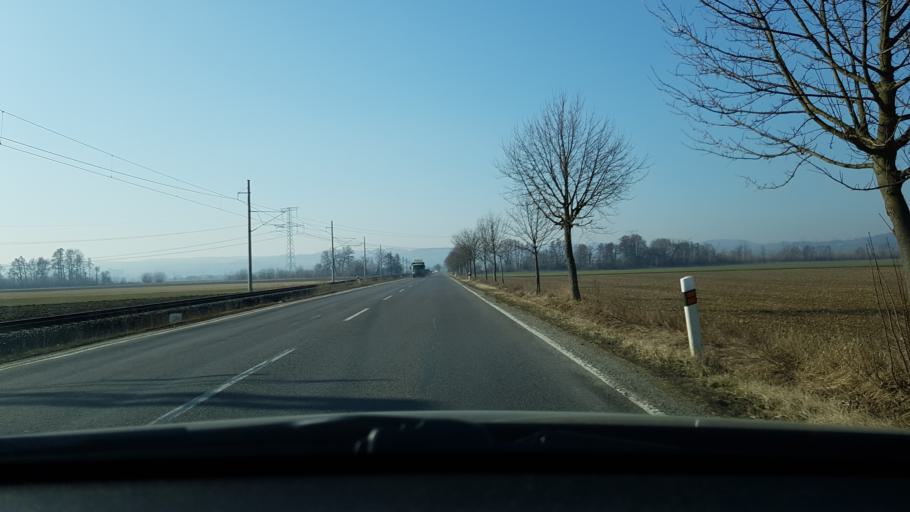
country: CZ
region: Olomoucky
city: Postrelmov
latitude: 49.8999
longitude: 16.9075
